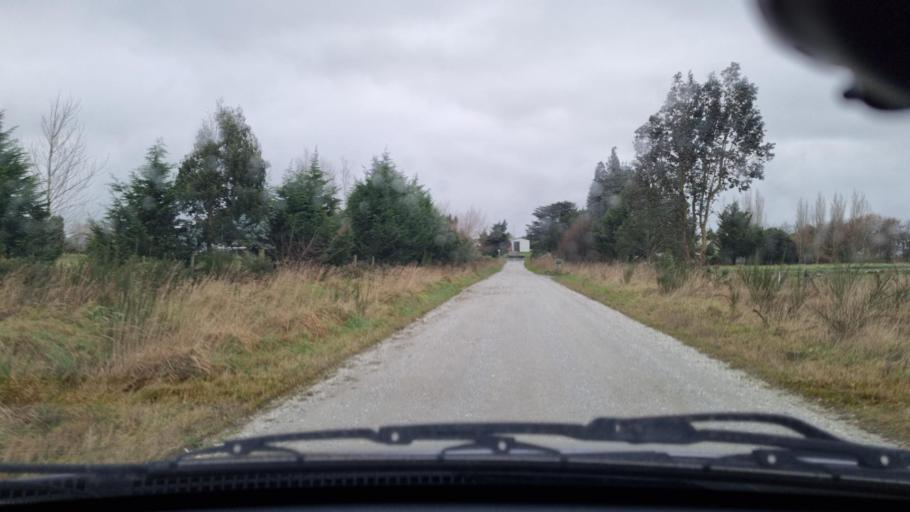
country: NZ
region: Southland
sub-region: Invercargill City
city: Invercargill
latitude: -46.4342
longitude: 168.3896
